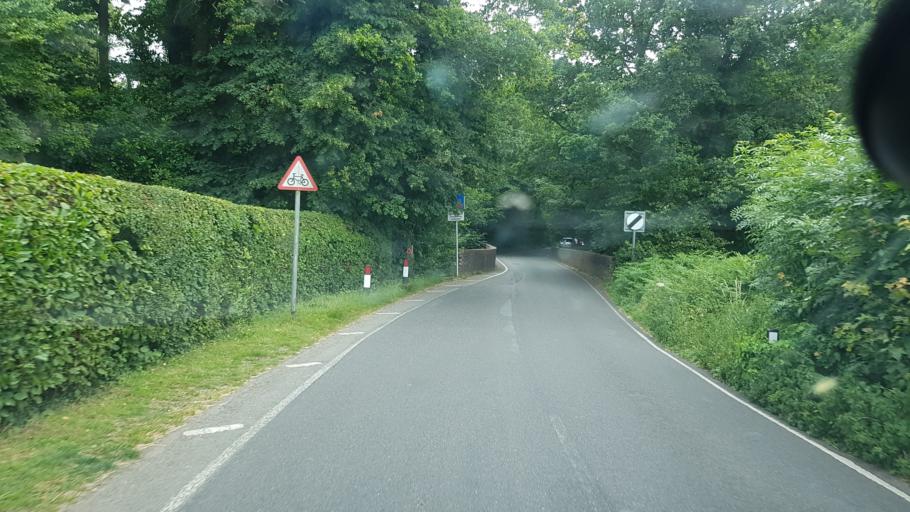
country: GB
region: England
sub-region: Surrey
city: Felbridge
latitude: 51.1268
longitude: -0.0342
